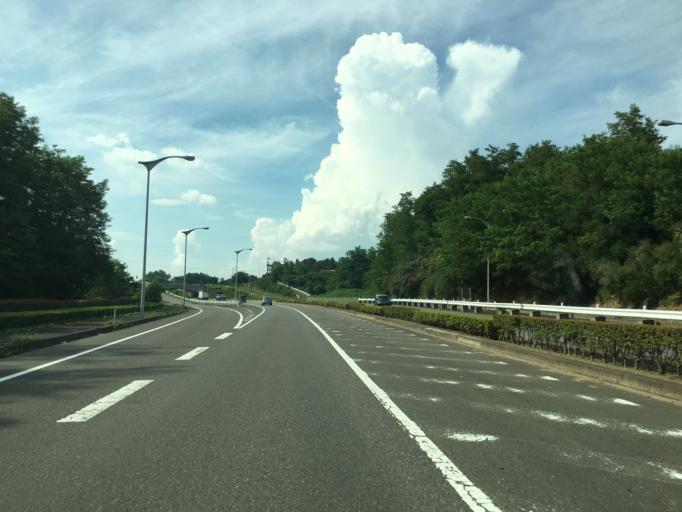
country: JP
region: Fukushima
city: Sukagawa
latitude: 37.2536
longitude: 140.4282
